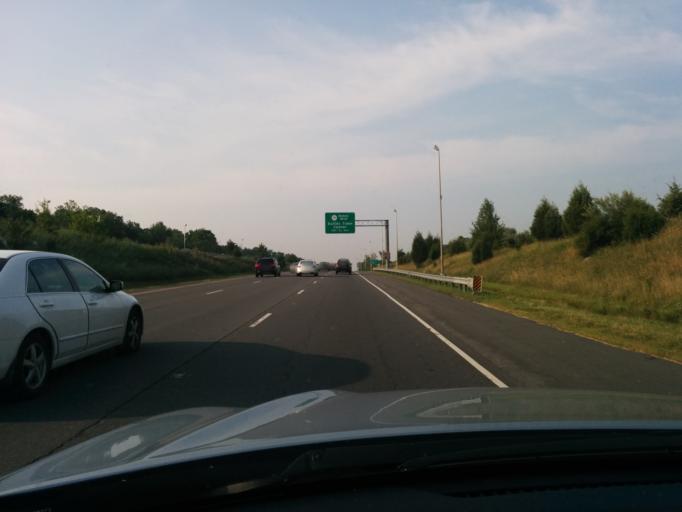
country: US
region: Virginia
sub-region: Loudoun County
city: Dulles Town Center
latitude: 39.0425
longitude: -77.4314
